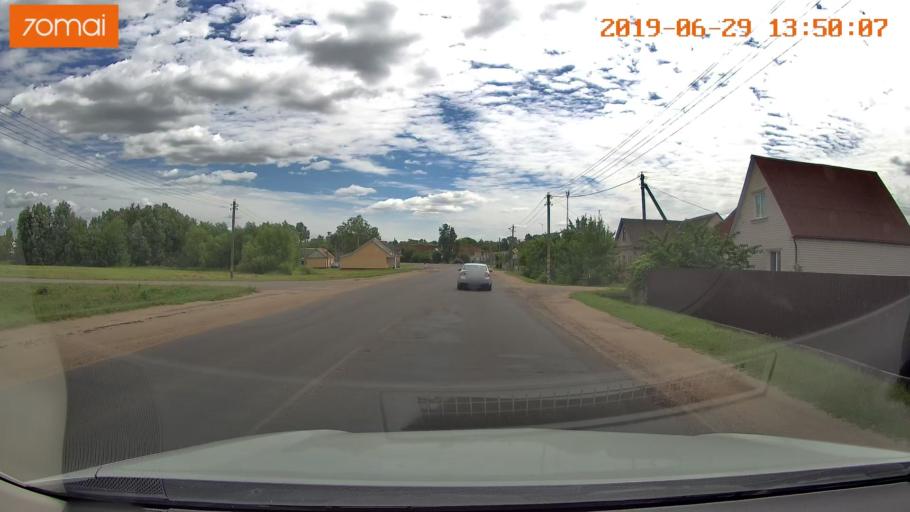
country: BY
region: Minsk
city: Slutsk
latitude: 53.0048
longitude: 27.5667
